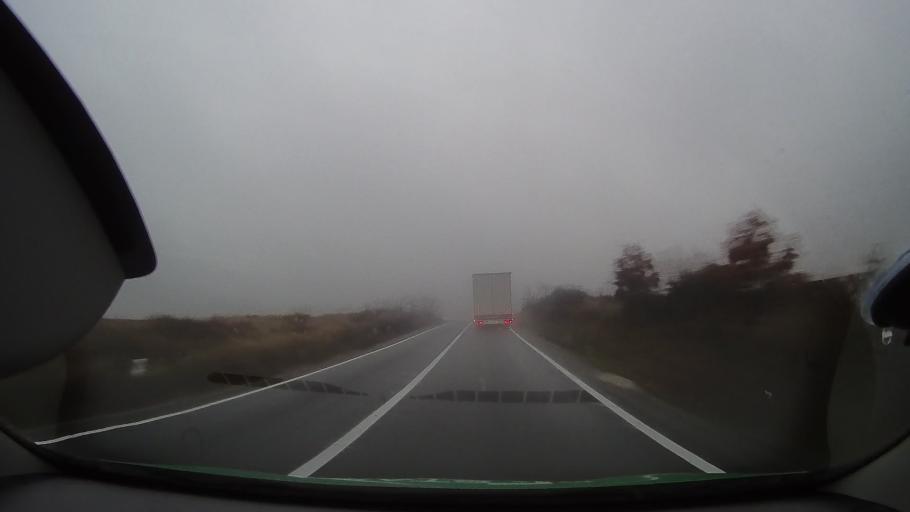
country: RO
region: Bihor
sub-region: Comuna Olcea
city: Calacea
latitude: 46.6570
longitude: 21.9608
